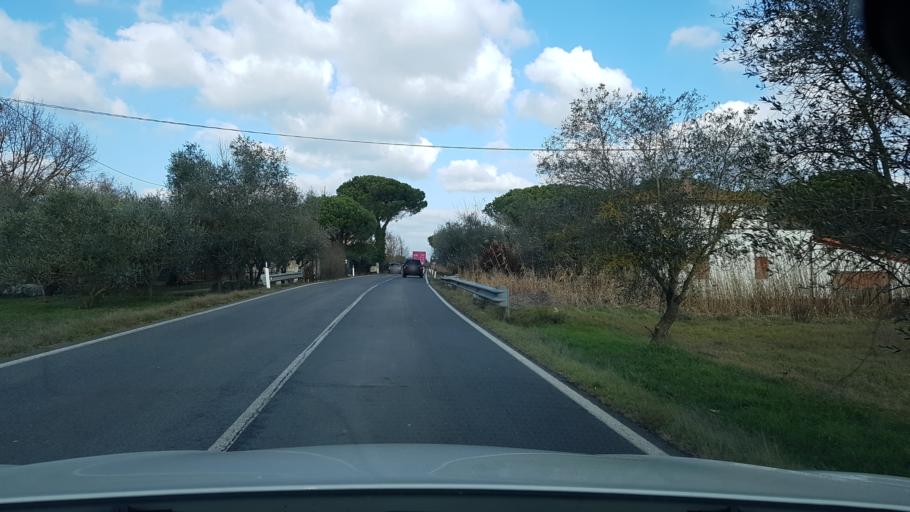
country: IT
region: Umbria
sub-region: Provincia di Perugia
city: Castiglione del Lago
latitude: 43.1596
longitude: 12.0167
